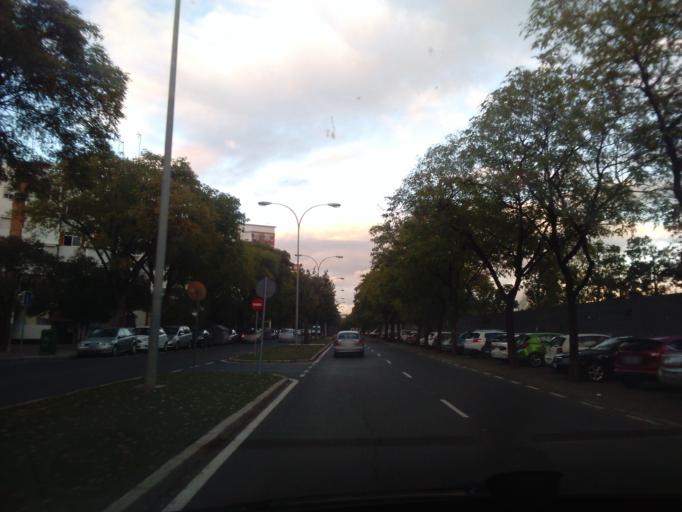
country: ES
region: Andalusia
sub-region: Provincia de Sevilla
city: Sevilla
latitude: 37.3909
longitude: -5.9657
